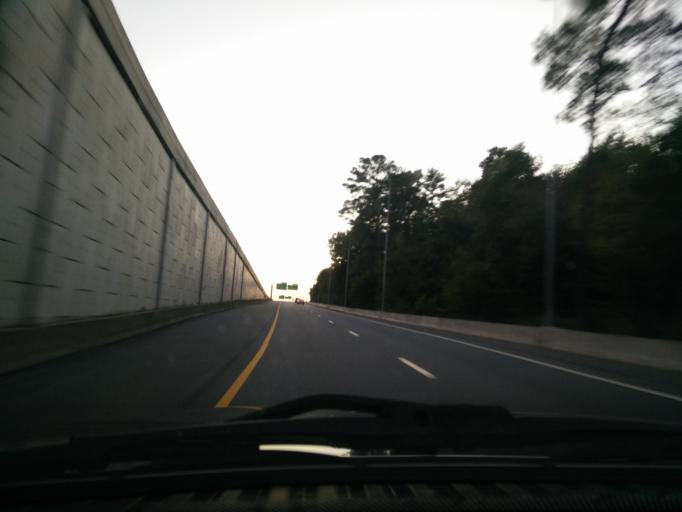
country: US
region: Virginia
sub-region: City of Chesapeake
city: Chesapeake
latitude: 36.7799
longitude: -76.2442
